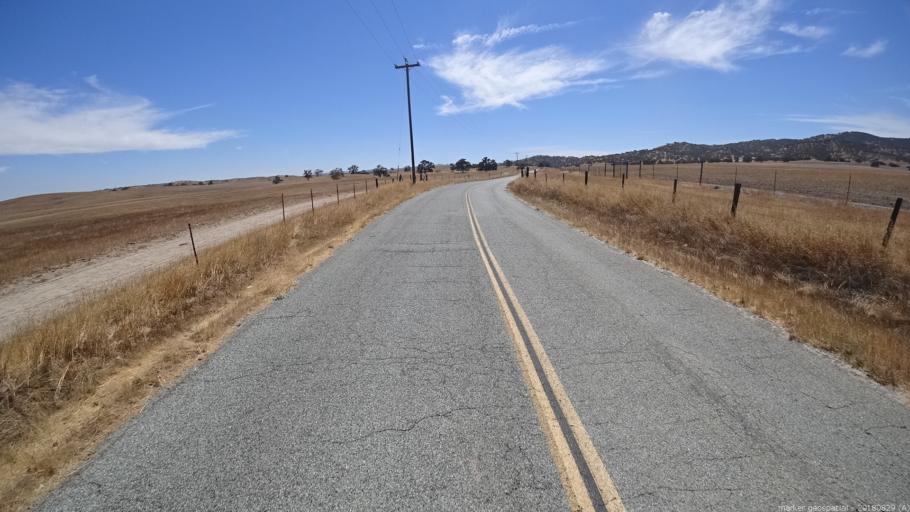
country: US
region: California
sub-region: San Luis Obispo County
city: Lake Nacimiento
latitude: 35.8429
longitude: -120.8424
